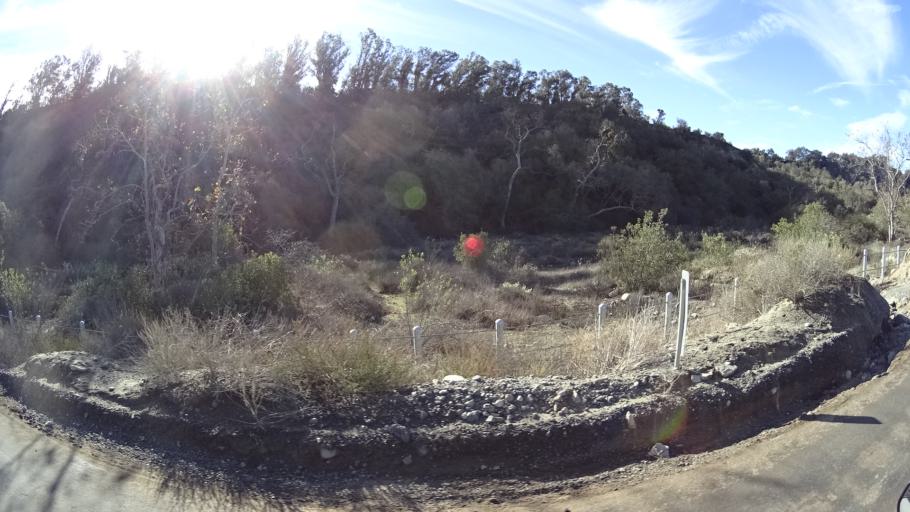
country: US
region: California
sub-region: Orange County
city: Trabuco Canyon
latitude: 33.6608
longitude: -117.5773
